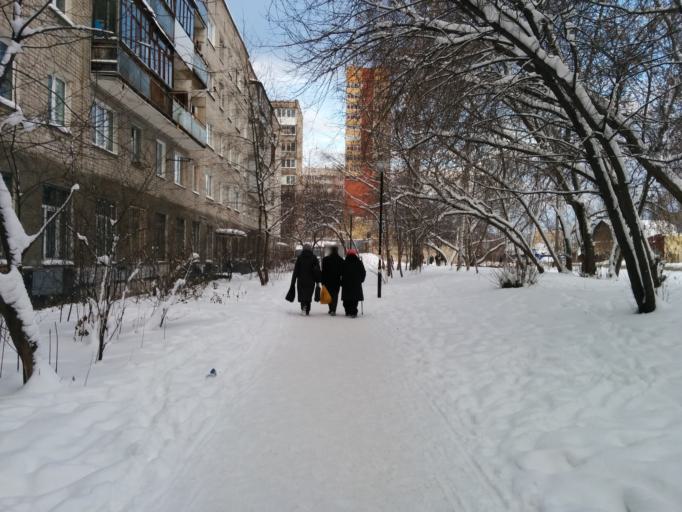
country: RU
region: Perm
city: Perm
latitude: 57.9846
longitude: 56.2915
